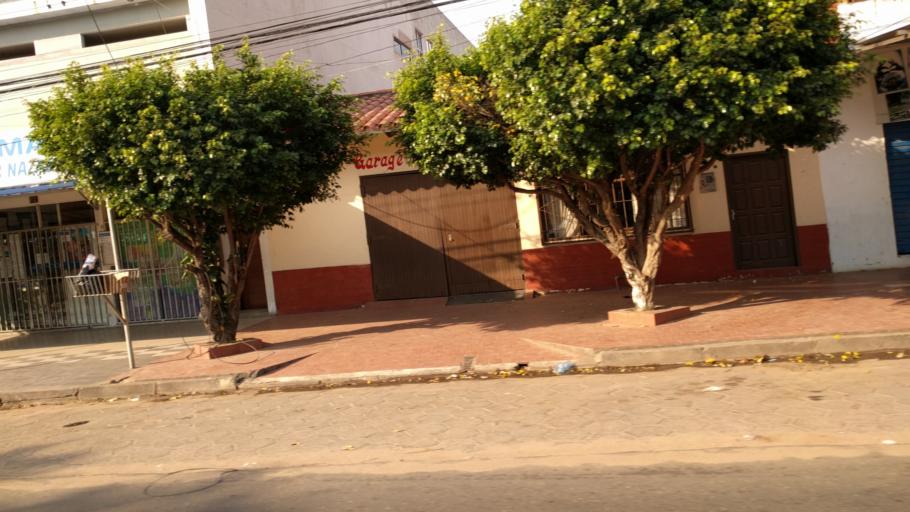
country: BO
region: Santa Cruz
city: Warnes
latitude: -17.5115
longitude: -63.1672
